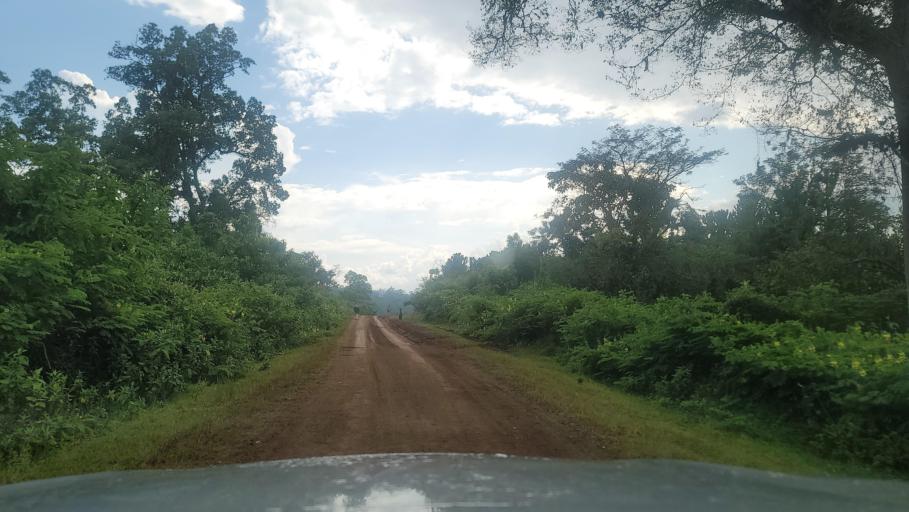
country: ET
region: Southern Nations, Nationalities, and People's Region
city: Bonga
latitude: 7.6349
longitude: 36.2244
